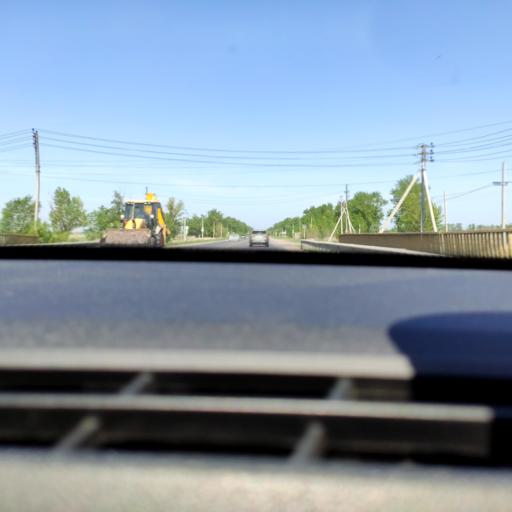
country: RU
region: Samara
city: Tol'yatti
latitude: 53.5861
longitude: 49.4050
